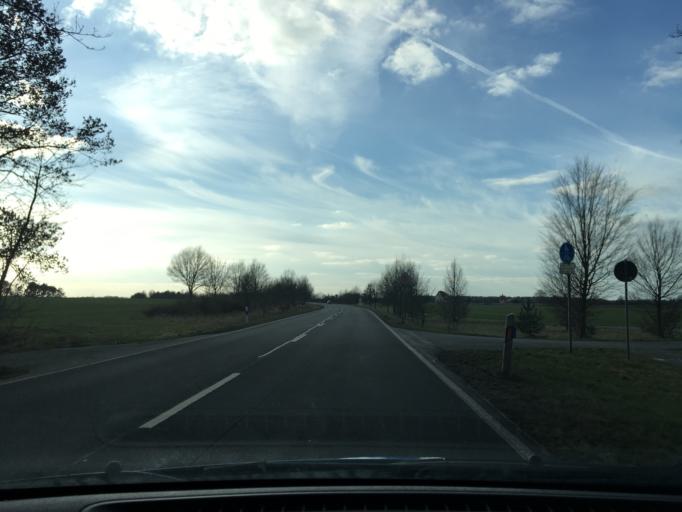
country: DE
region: Saxony-Anhalt
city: Luftkurort Arendsee
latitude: 52.8840
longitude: 11.5412
